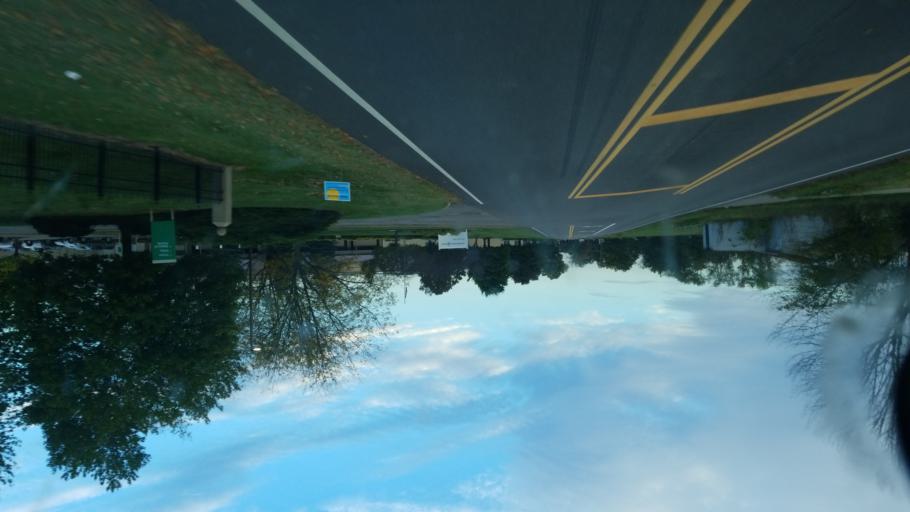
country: US
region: Ohio
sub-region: Knox County
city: Mount Vernon
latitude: 40.3649
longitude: -82.4913
